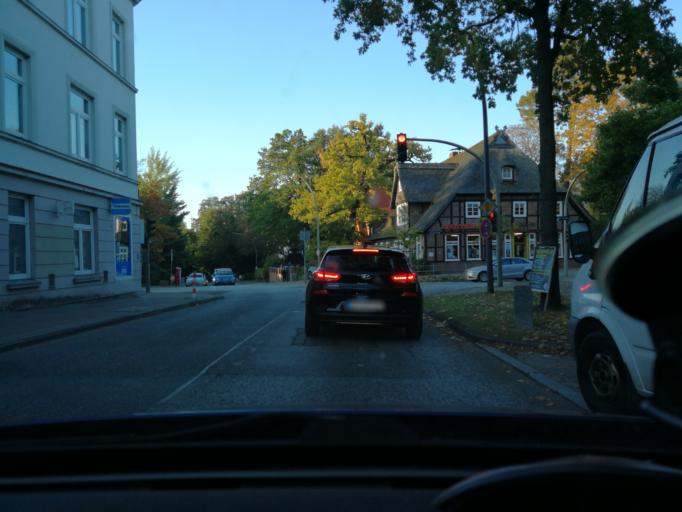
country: DE
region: Hamburg
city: Harburg
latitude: 53.4637
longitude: 9.9565
